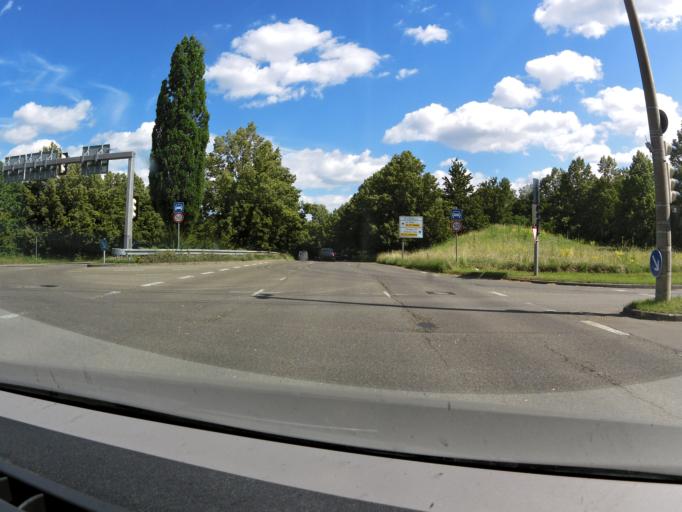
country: DE
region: Baden-Wuerttemberg
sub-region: Regierungsbezirk Stuttgart
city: Leinfelden-Echterdingen
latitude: 48.7237
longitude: 9.1669
